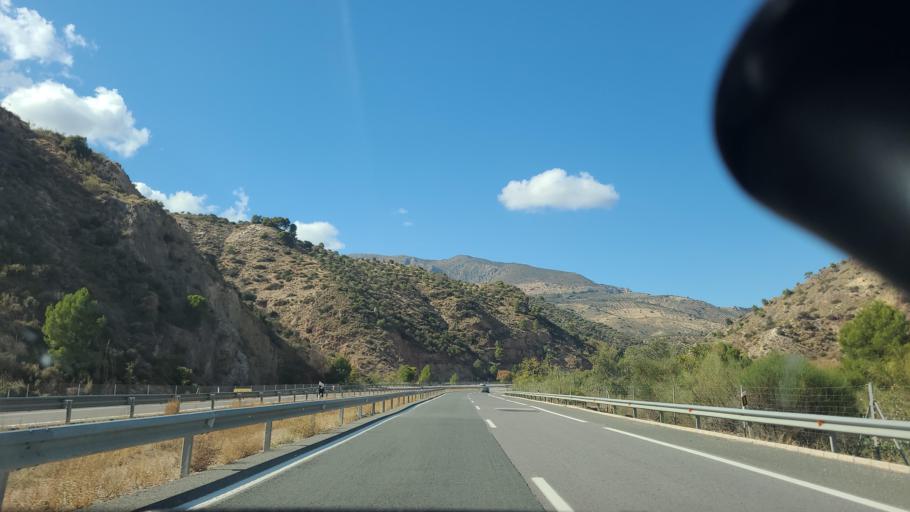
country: ES
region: Andalusia
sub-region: Provincia de Jaen
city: Cambil
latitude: 37.6584
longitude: -3.6087
